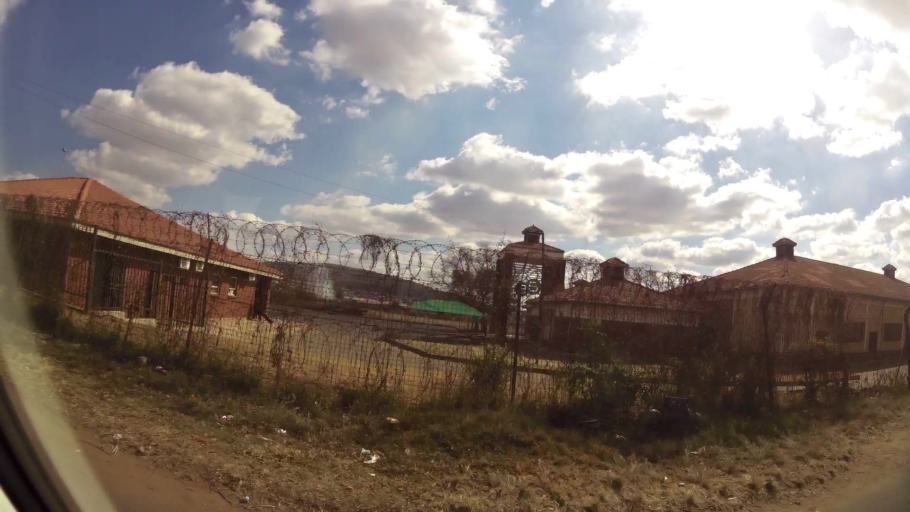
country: ZA
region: Gauteng
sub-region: City of Tshwane Metropolitan Municipality
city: Cullinan
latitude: -25.7063
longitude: 28.4012
